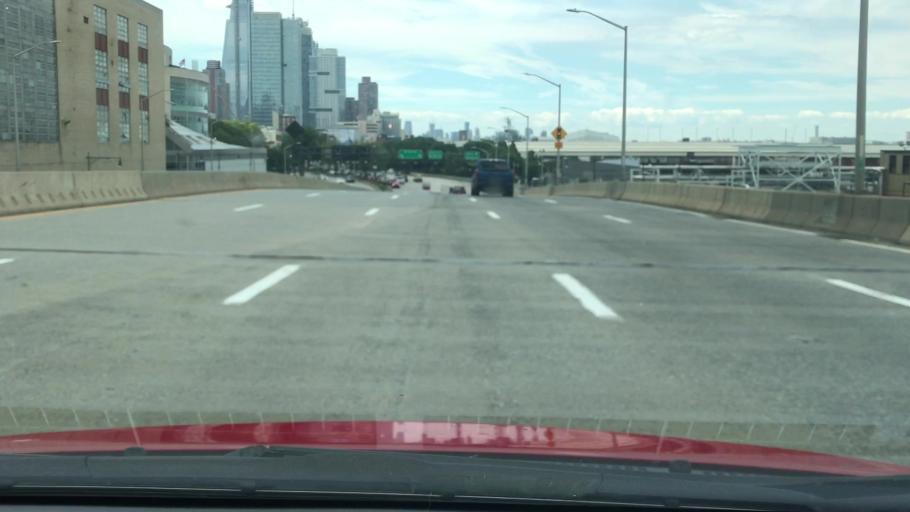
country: US
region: New Jersey
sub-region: Hudson County
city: Guttenberg
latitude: 40.7732
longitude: -73.9932
